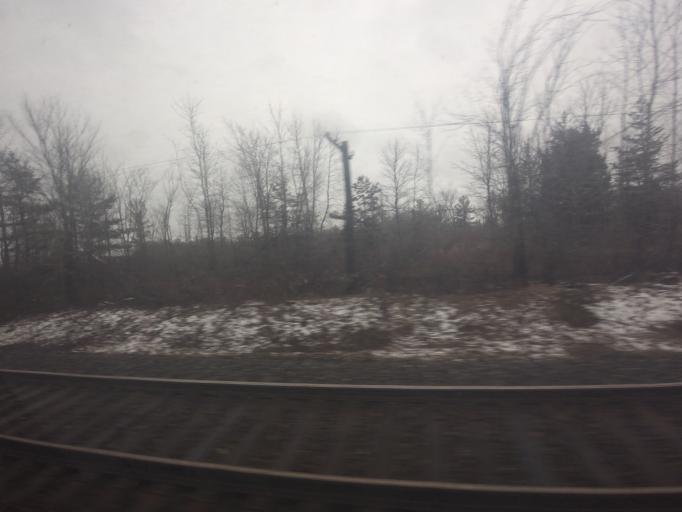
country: CA
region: Ontario
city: Kingston
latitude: 44.2289
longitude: -76.6692
